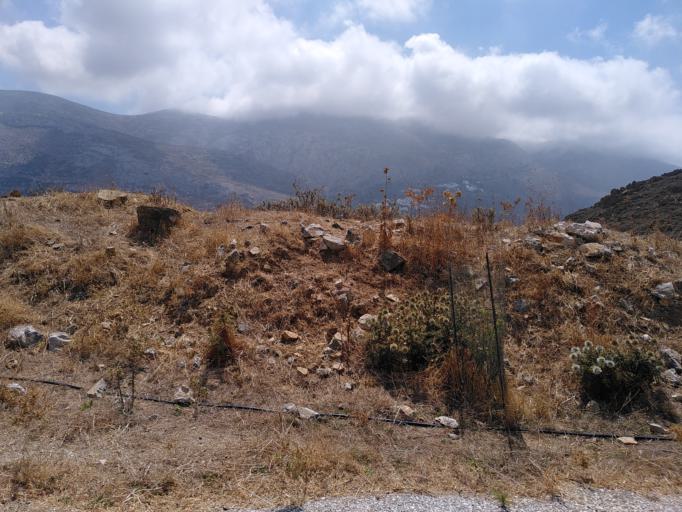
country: GR
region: South Aegean
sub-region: Nomos Kykladon
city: Amorgos
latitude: 36.9133
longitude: 25.9776
